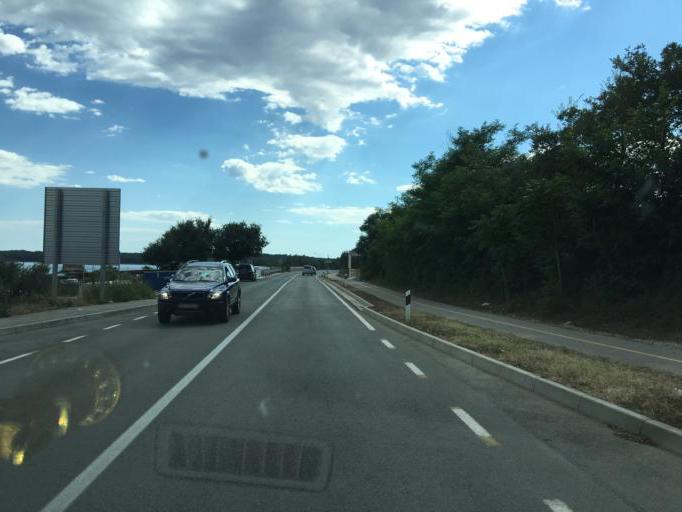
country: HR
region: Primorsko-Goranska
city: Punat
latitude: 45.0394
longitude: 14.6192
